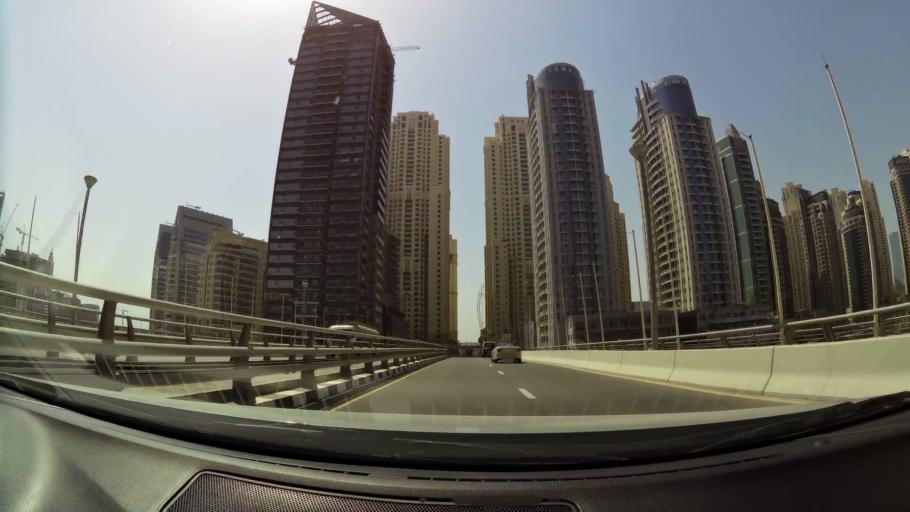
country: AE
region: Dubai
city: Dubai
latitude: 25.0710
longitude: 55.1334
